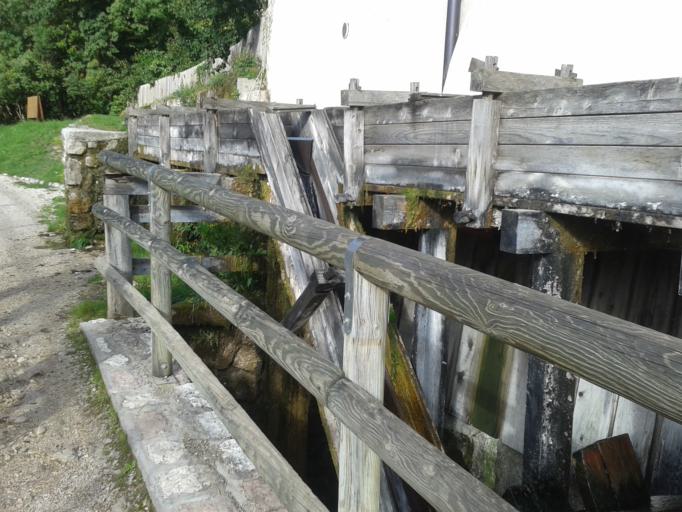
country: IT
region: Trentino-Alto Adige
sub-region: Provincia di Trento
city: Fondo
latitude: 46.4391
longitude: 11.1387
